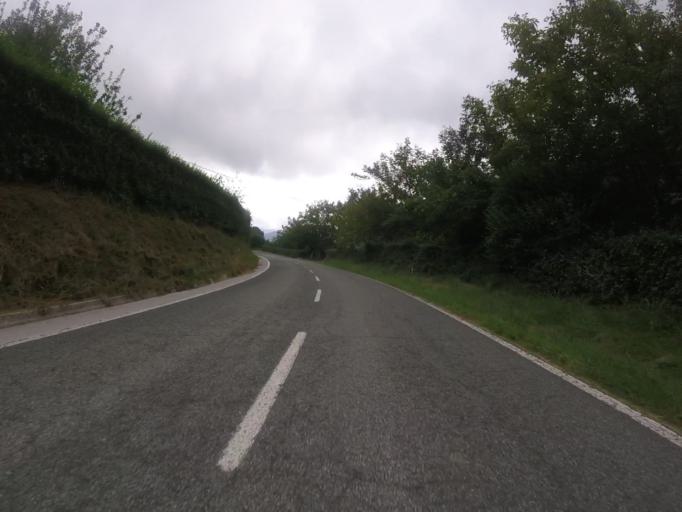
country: ES
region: Navarre
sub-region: Provincia de Navarra
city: Ezkurra
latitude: 43.0827
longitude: -1.8373
